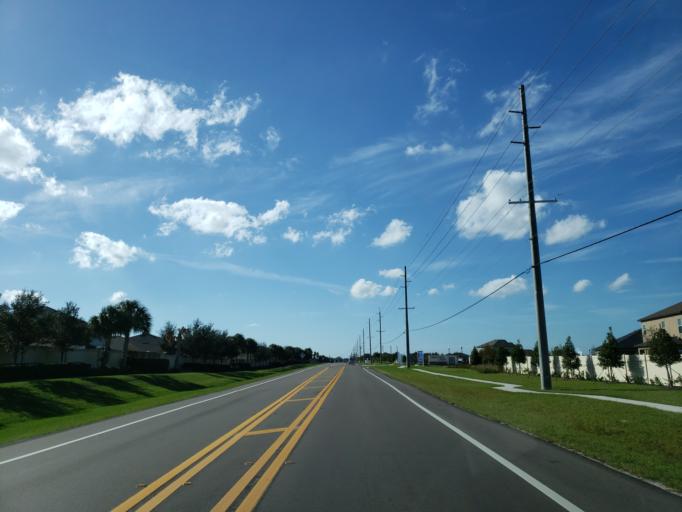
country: US
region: Florida
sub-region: Hillsborough County
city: Riverview
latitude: 27.8216
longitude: -82.3145
